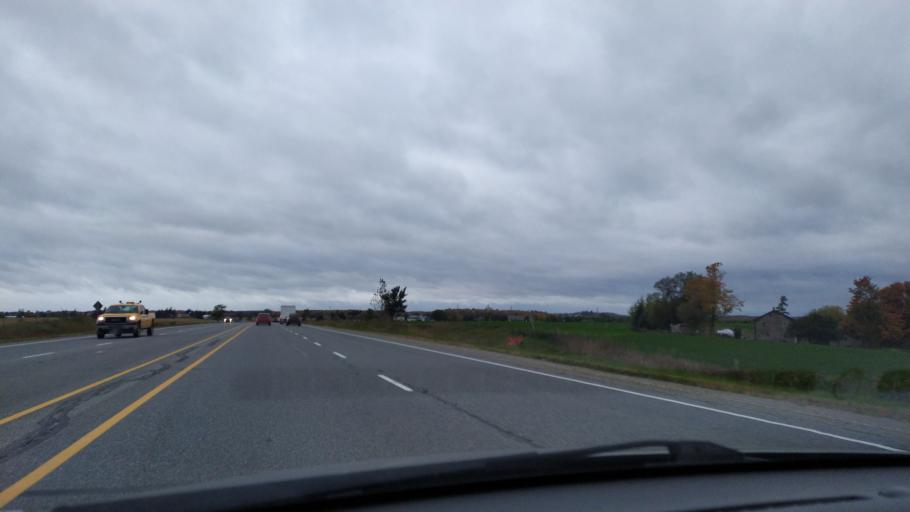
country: CA
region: Ontario
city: Kitchener
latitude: 43.3644
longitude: -80.7254
